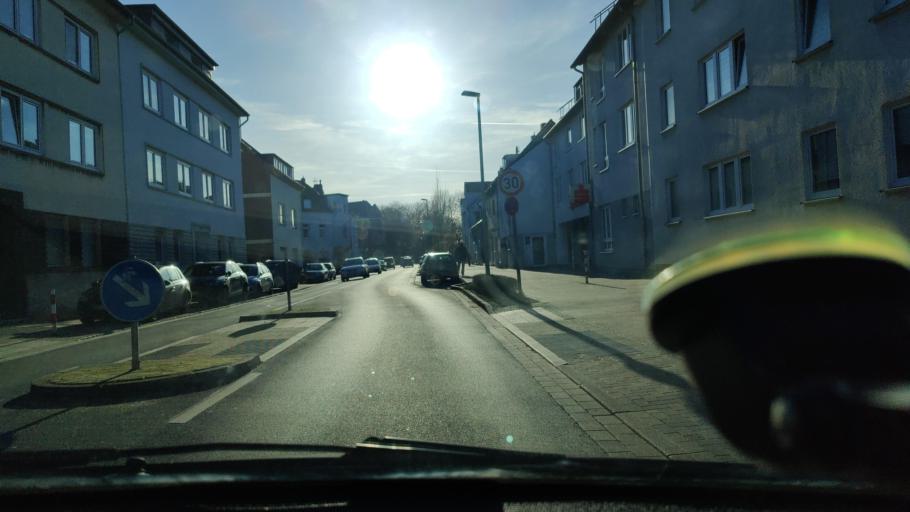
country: DE
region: North Rhine-Westphalia
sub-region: Regierungsbezirk Arnsberg
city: Herne
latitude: 51.5606
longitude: 7.2308
